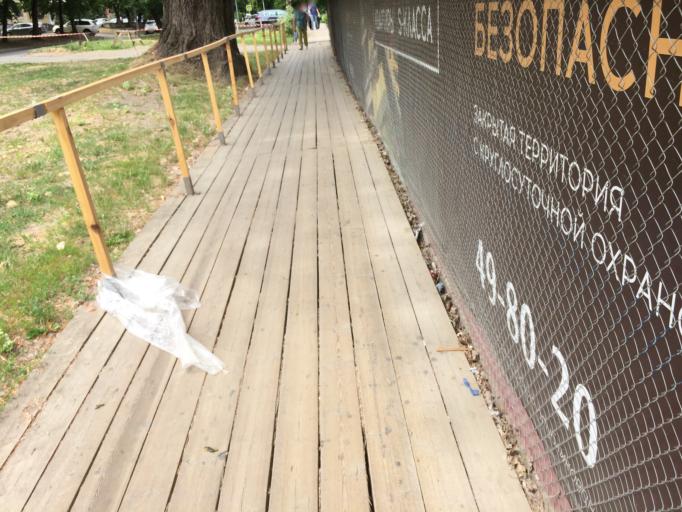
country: RU
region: Stavropol'skiy
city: Stavropol'
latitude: 45.0407
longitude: 41.9563
